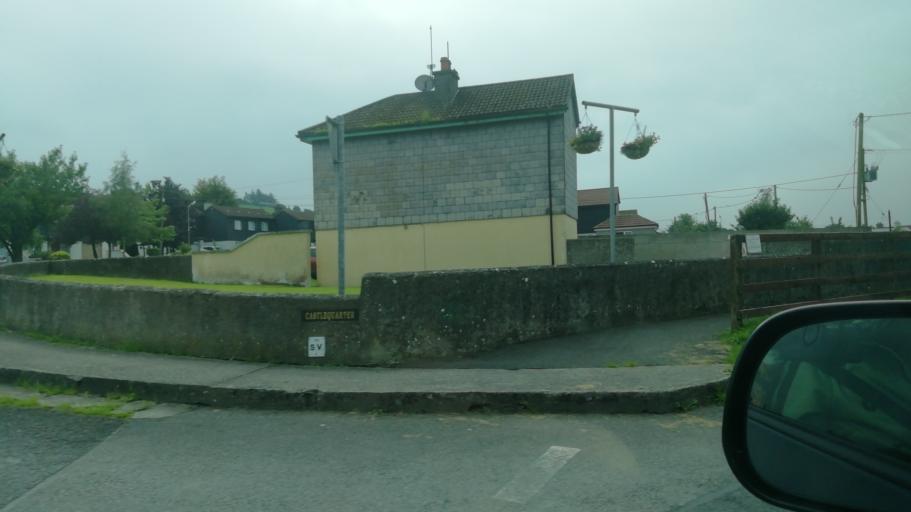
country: IE
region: Munster
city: Fethard
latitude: 52.5710
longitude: -7.6655
